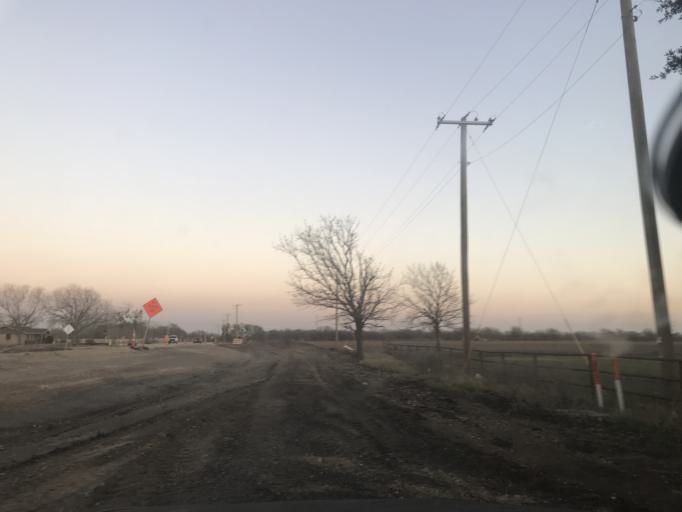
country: US
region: Texas
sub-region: Williamson County
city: Hutto
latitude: 30.5137
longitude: -97.5337
